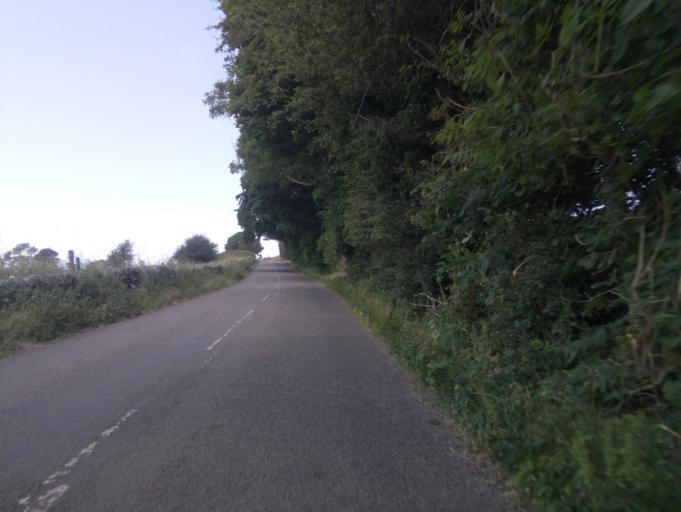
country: GB
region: England
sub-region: Derbyshire
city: Tideswell
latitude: 53.2591
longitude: -1.8027
